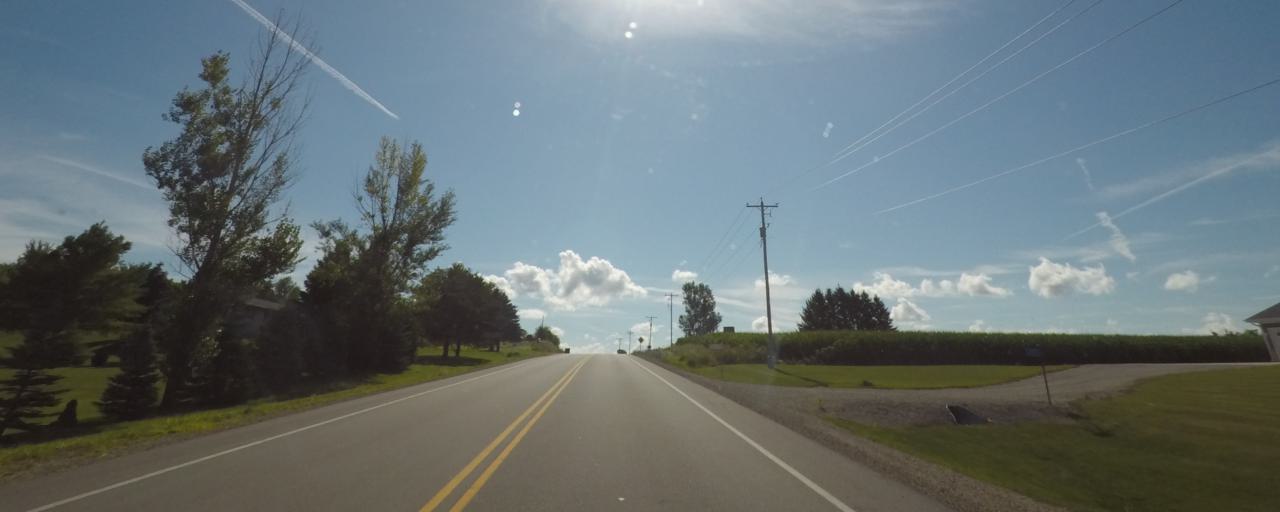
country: US
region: Wisconsin
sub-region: Jefferson County
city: Ixonia
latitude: 43.0727
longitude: -88.6491
